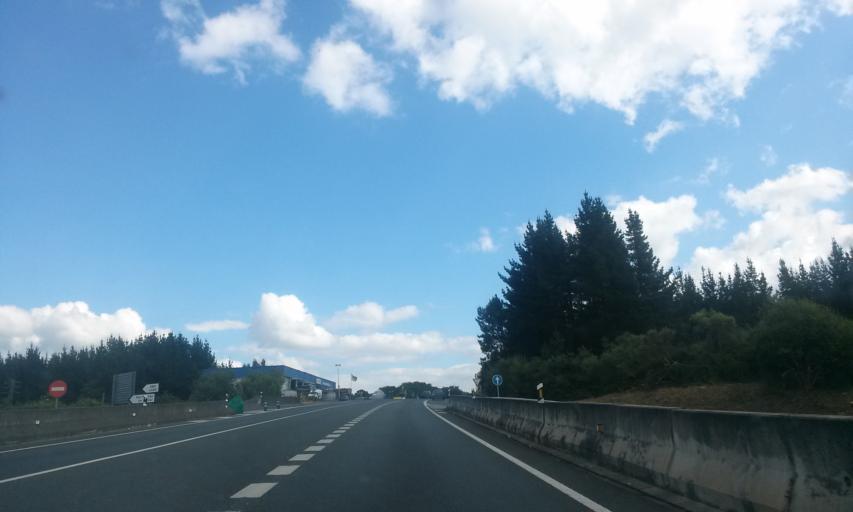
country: ES
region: Galicia
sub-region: Provincia de Lugo
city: Outeiro de Rei
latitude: 43.0595
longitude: -7.5993
